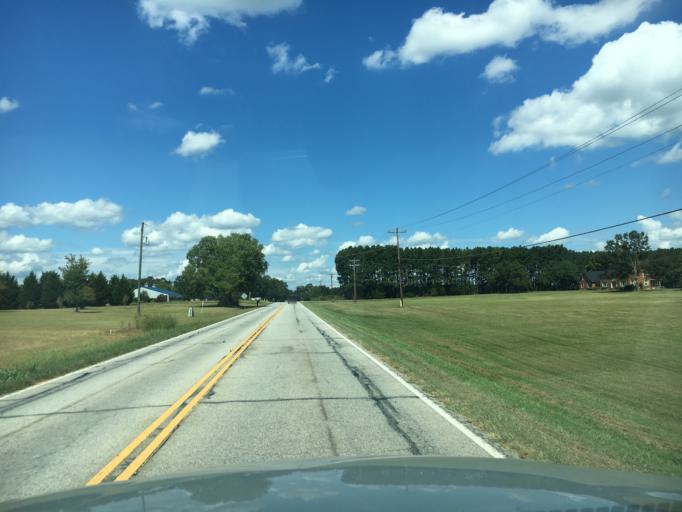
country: US
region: South Carolina
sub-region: Laurens County
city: Laurens
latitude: 34.5022
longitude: -82.0733
